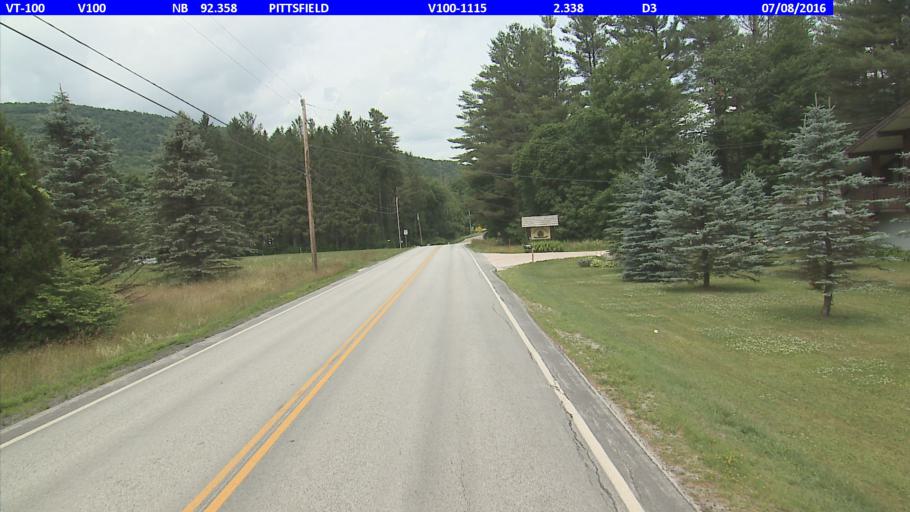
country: US
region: Vermont
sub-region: Rutland County
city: Rutland
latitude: 43.7507
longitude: -72.8206
